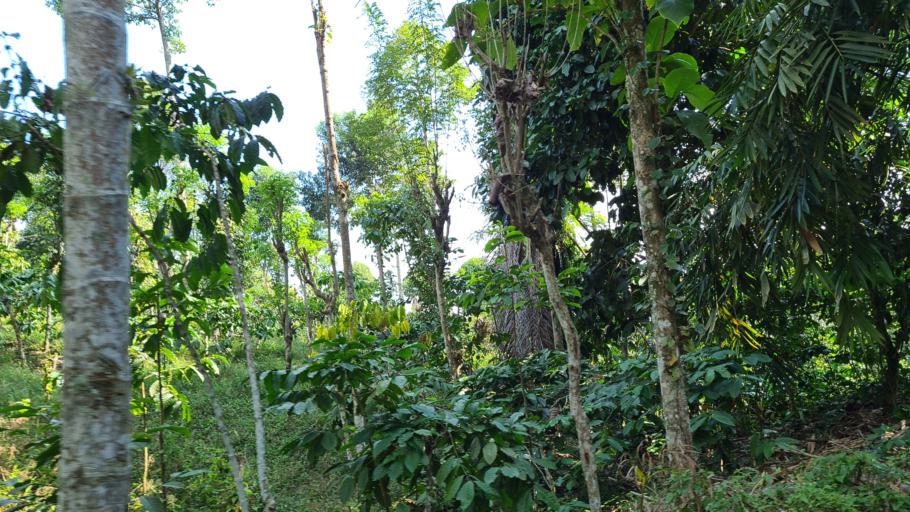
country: ID
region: Lampung
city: Kuripan
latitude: -5.0694
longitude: 103.8693
